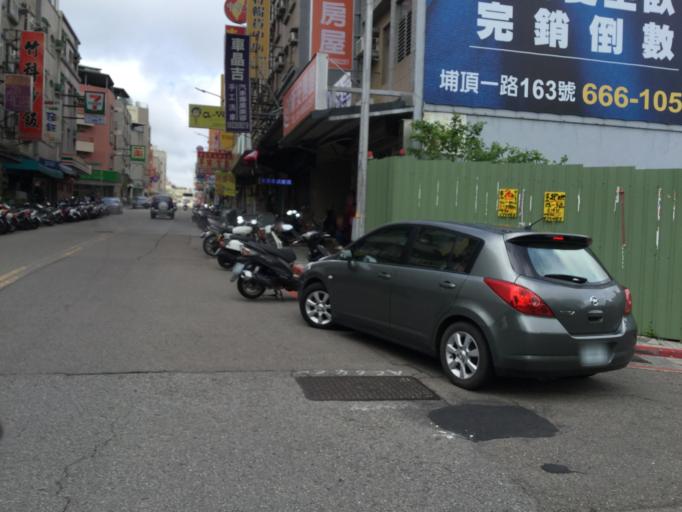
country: TW
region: Taiwan
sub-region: Hsinchu
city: Hsinchu
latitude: 24.7766
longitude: 121.0246
